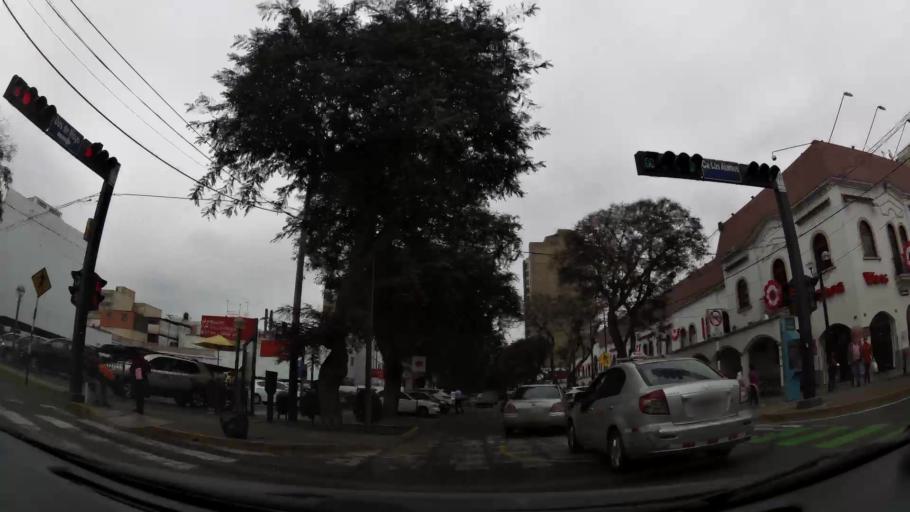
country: PE
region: Lima
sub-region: Lima
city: San Isidro
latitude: -12.0918
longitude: -77.0422
